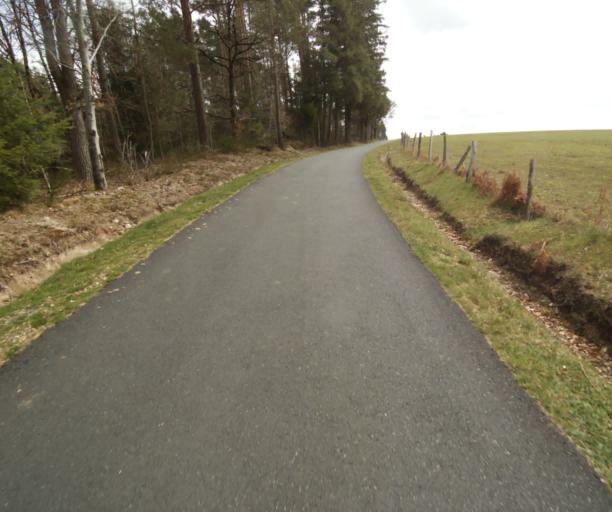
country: FR
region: Limousin
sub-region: Departement de la Correze
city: Correze
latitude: 45.3427
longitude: 1.9532
